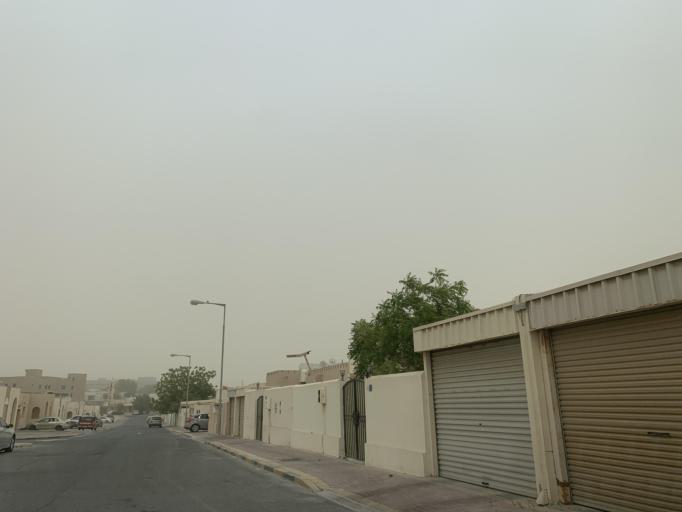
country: BH
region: Central Governorate
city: Madinat Hamad
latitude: 26.1341
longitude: 50.5196
